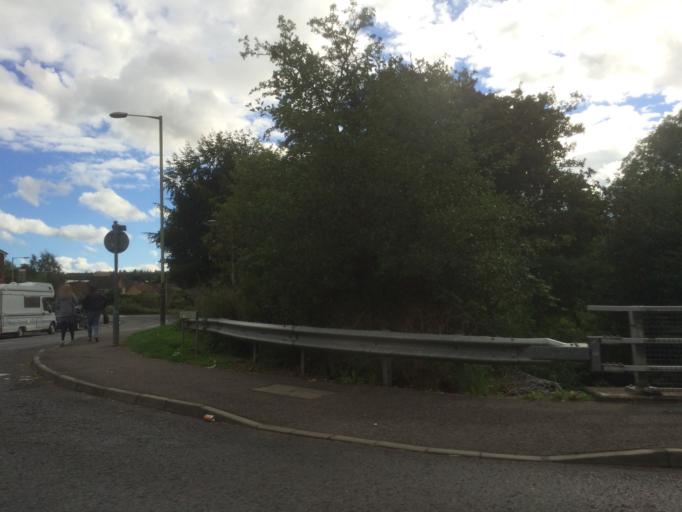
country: GB
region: Scotland
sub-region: Perth and Kinross
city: Luncarty
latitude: 56.4144
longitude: -3.4675
